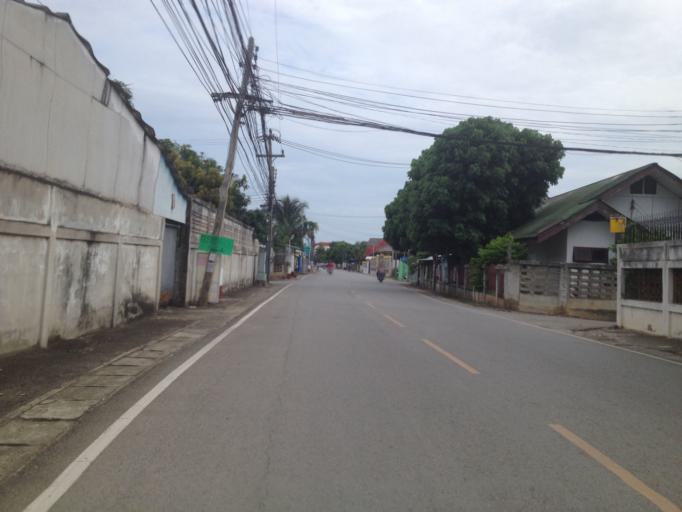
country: TH
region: Chiang Mai
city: Hang Dong
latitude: 18.6929
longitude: 98.9181
